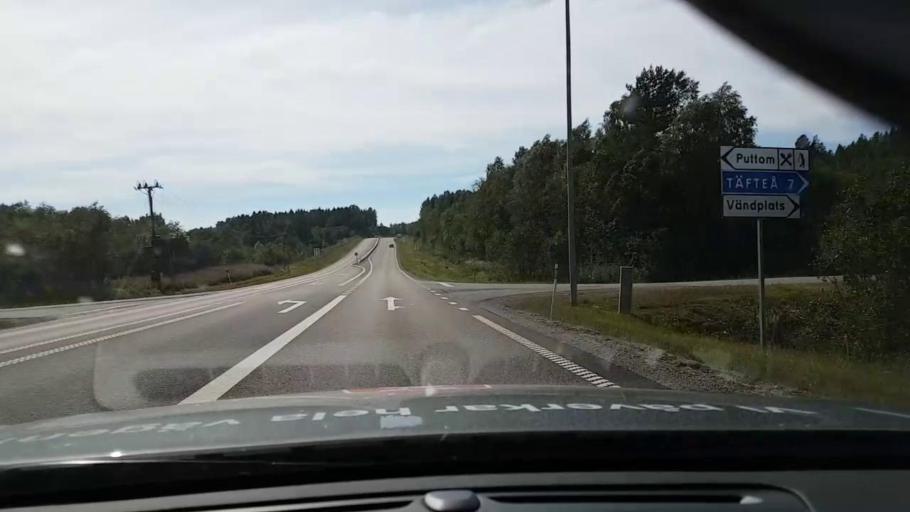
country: SE
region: Vaesternorrland
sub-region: OErnskoeldsviks Kommun
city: Ornskoldsvik
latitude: 63.3113
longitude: 18.9350
